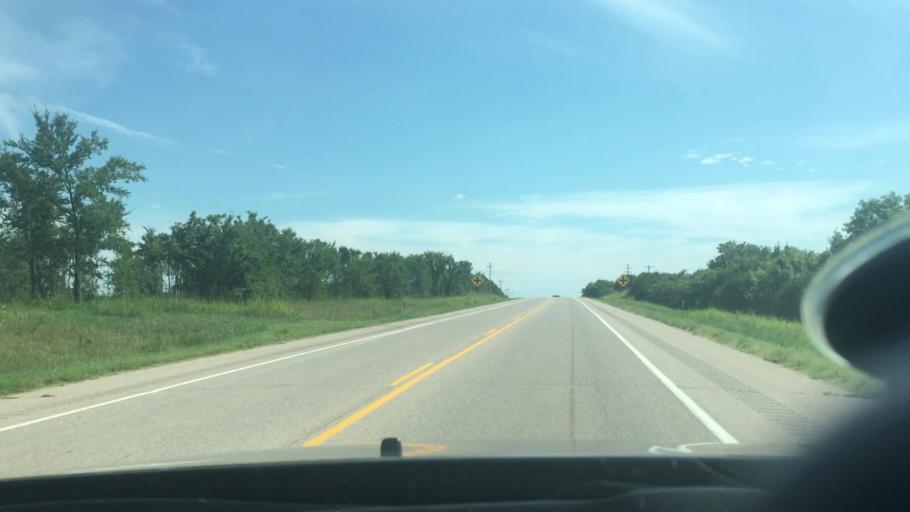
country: US
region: Oklahoma
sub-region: Seminole County
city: Konawa
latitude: 34.9882
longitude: -96.6793
